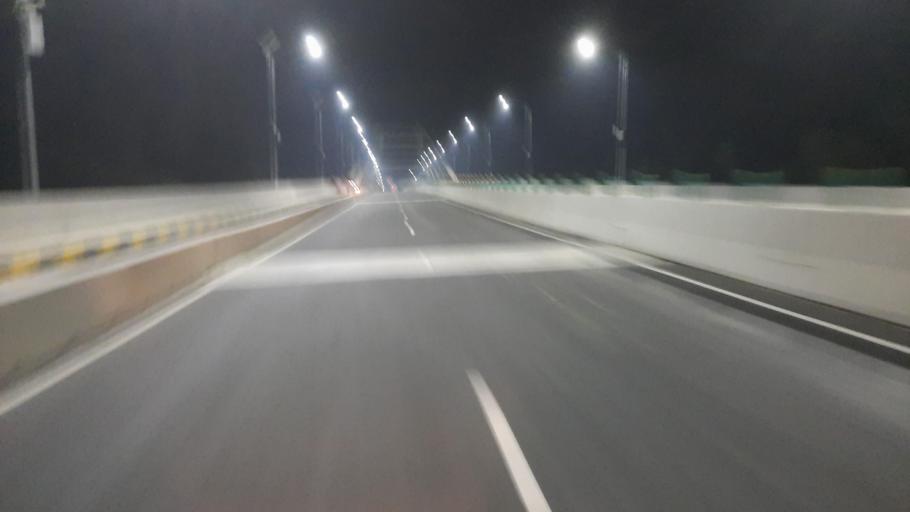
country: BD
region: Khulna
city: Kalia
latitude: 23.1911
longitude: 89.6926
